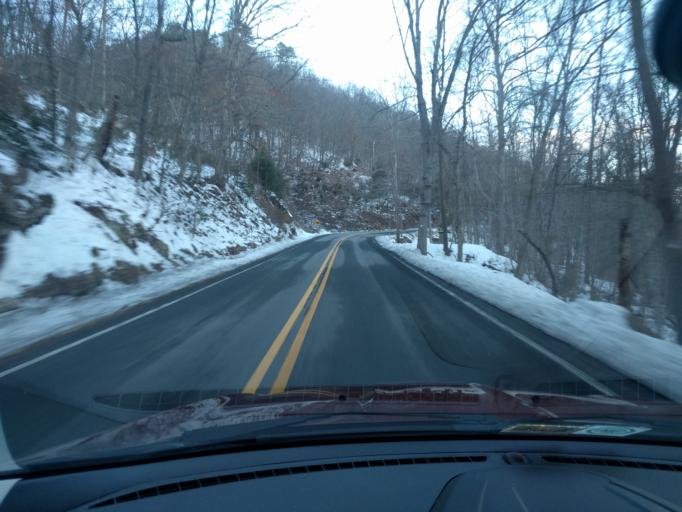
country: US
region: Virginia
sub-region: Bath County
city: Warm Springs
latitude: 38.0804
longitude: -79.8452
